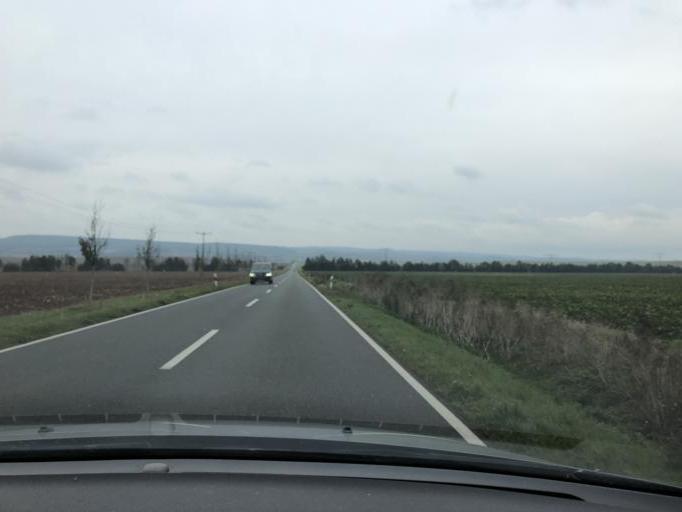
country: DE
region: Saxony-Anhalt
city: Kelbra
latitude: 51.4397
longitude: 11.0519
